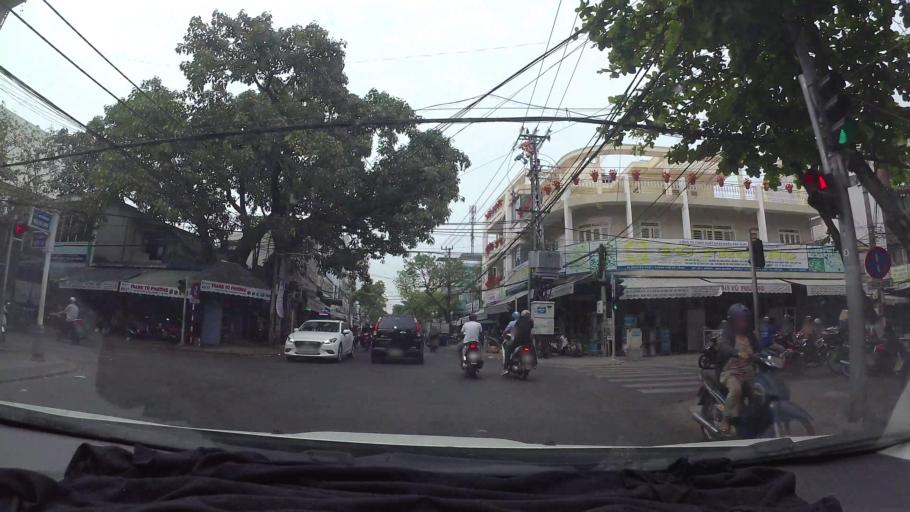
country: VN
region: Da Nang
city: Da Nang
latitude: 16.0648
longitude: 108.2165
